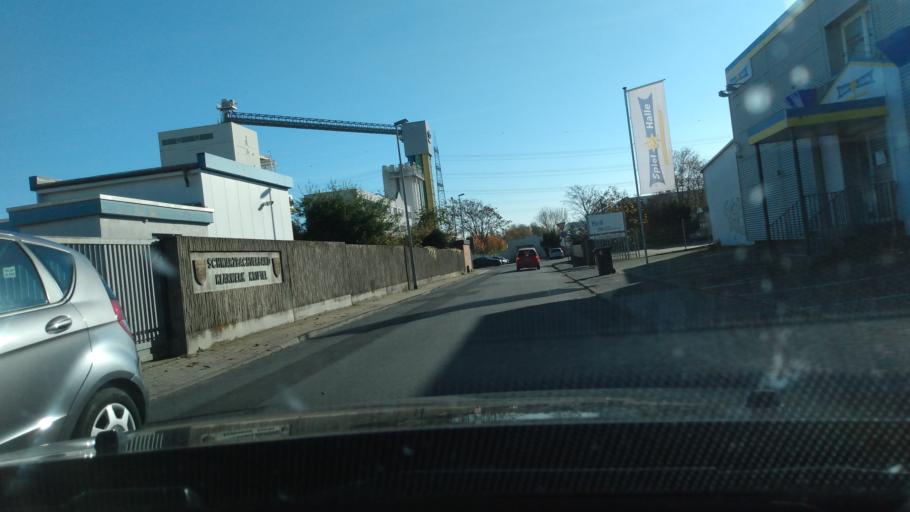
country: DE
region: Hesse
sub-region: Regierungsbezirk Darmstadt
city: Hattersheim
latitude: 50.0788
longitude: 8.4737
